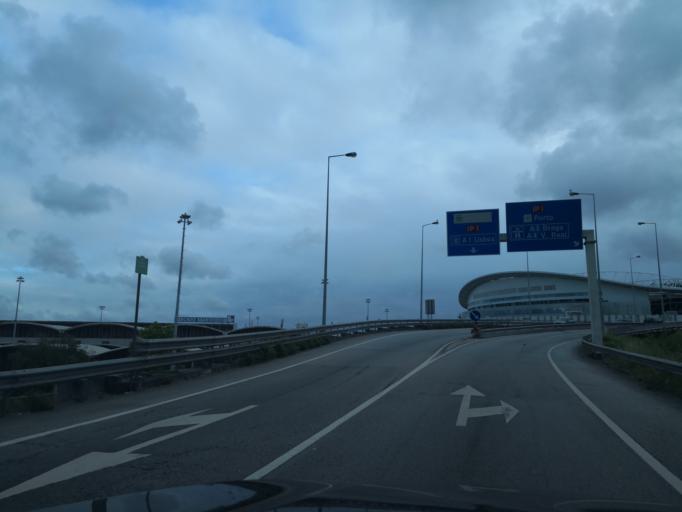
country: PT
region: Porto
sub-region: Gondomar
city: Rio Tinto
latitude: 41.1646
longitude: -8.5791
